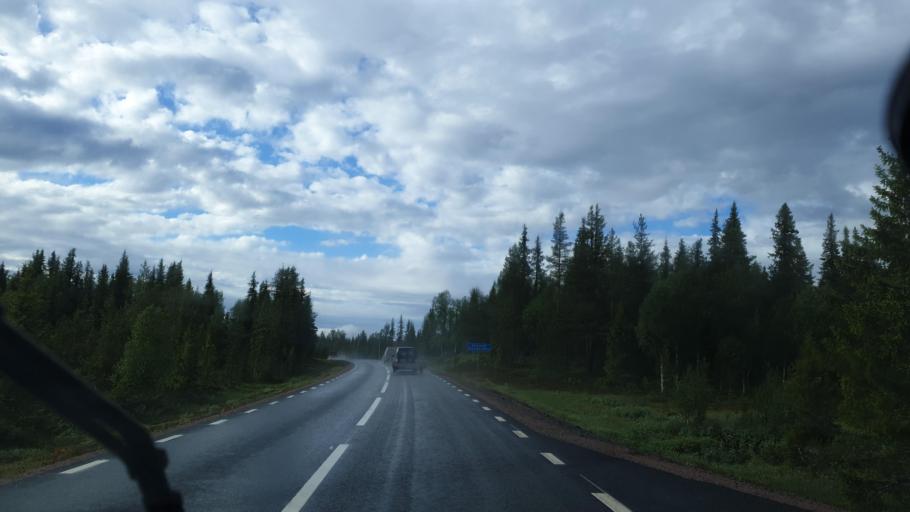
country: SE
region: Norrbotten
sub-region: Arjeplogs Kommun
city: Arjeplog
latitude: 65.8778
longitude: 18.4062
